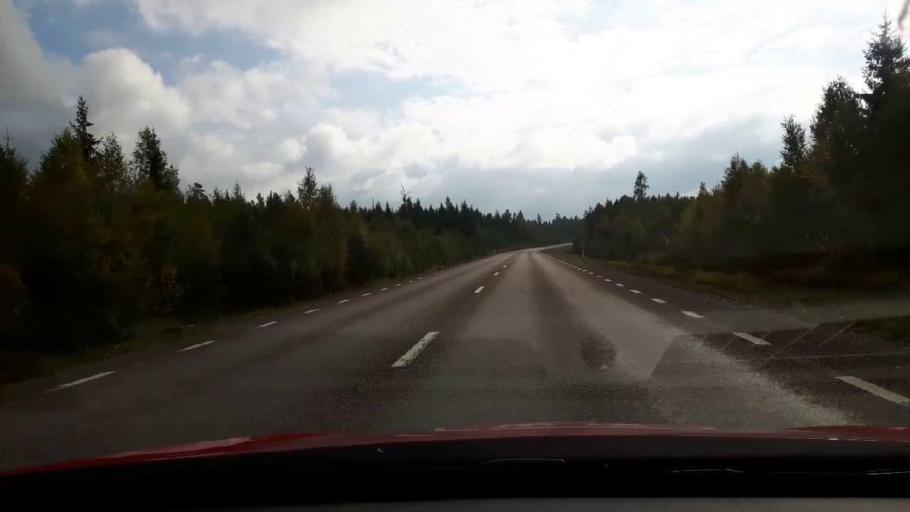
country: SE
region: Gaevleborg
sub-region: Gavle Kommun
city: Norrsundet
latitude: 61.0832
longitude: 16.9601
